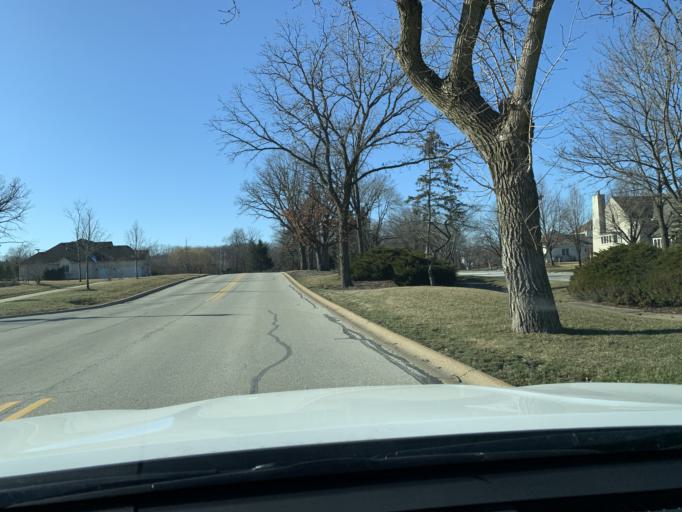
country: US
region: Illinois
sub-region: DuPage County
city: Burr Ridge
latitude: 41.7308
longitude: -87.9324
